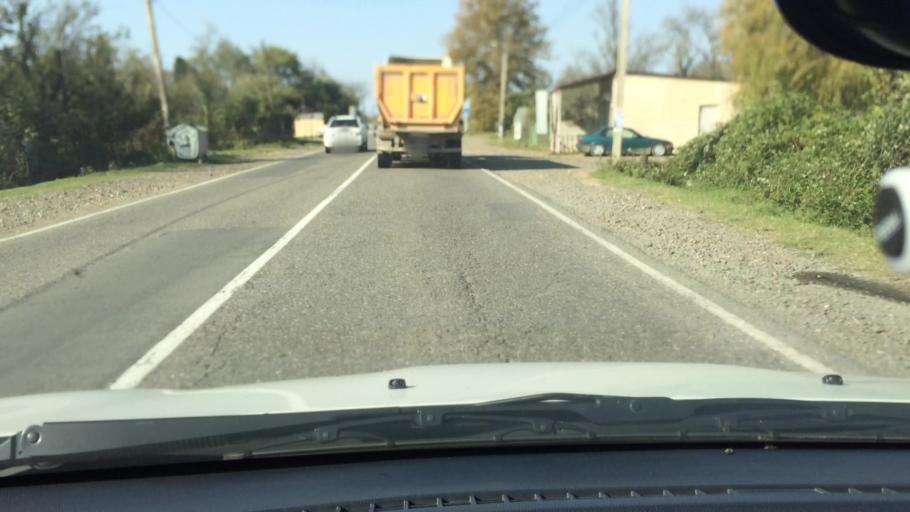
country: GE
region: Guria
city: Lanchkhuti
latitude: 42.0867
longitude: 42.0121
